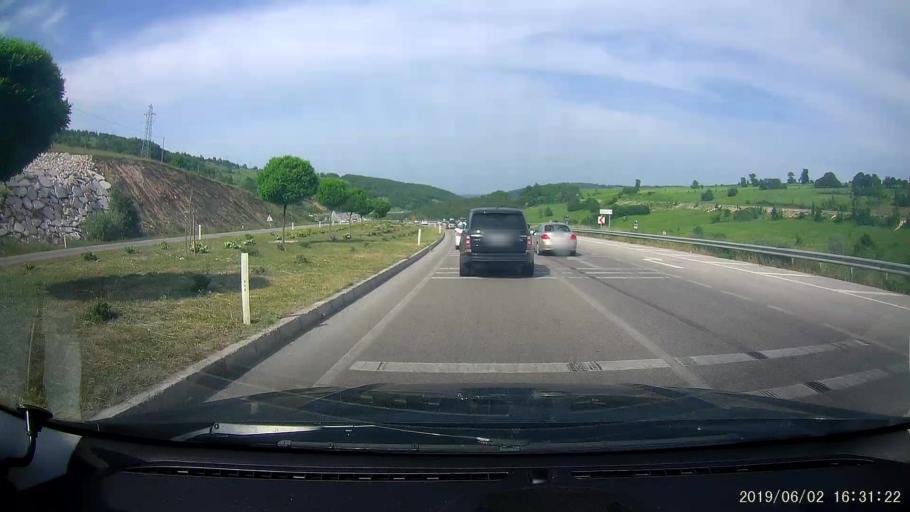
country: TR
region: Samsun
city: Ladik
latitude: 41.0316
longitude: 35.9004
